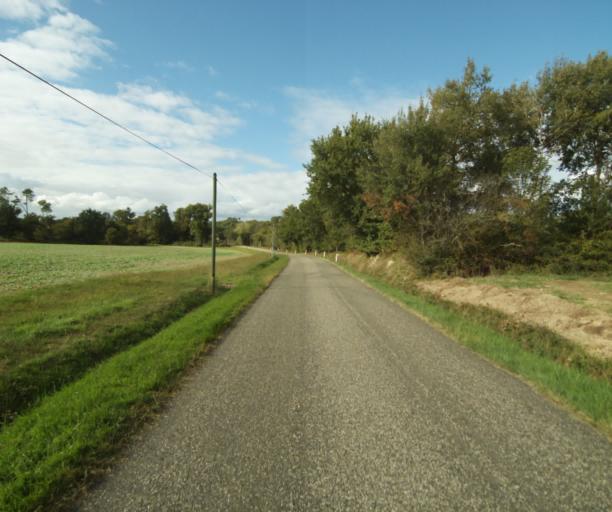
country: FR
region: Midi-Pyrenees
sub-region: Departement du Gers
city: Eauze
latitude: 43.9138
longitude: 0.0963
